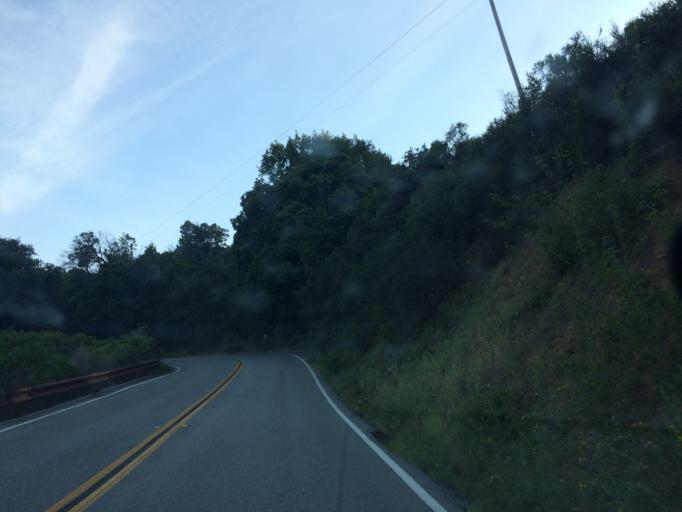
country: US
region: California
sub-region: Santa Clara County
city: Los Altos Hills
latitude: 37.3477
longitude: -122.1756
